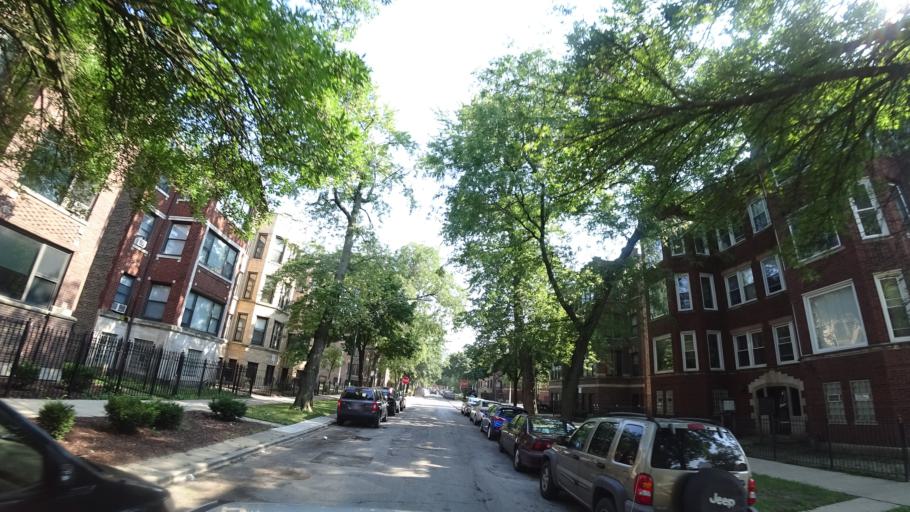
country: US
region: Illinois
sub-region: Cook County
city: Chicago
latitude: 41.7721
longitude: -87.5826
